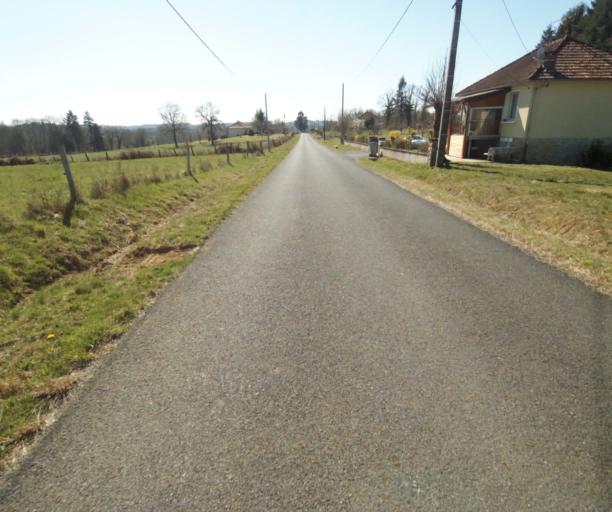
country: FR
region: Limousin
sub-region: Departement de la Correze
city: Saint-Mexant
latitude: 45.3176
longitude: 1.6465
